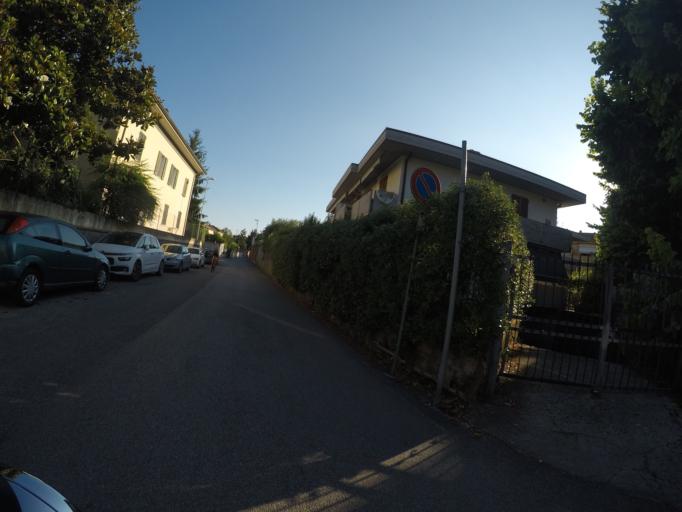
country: IT
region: Tuscany
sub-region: Provincia di Massa-Carrara
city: Massa
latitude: 44.0330
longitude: 10.1390
